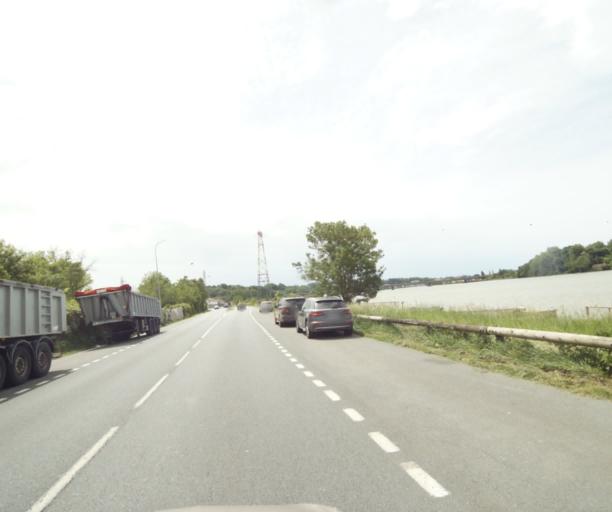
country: FR
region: Aquitaine
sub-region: Departement des Pyrenees-Atlantiques
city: Mouguerre
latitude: 43.4862
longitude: -1.4391
